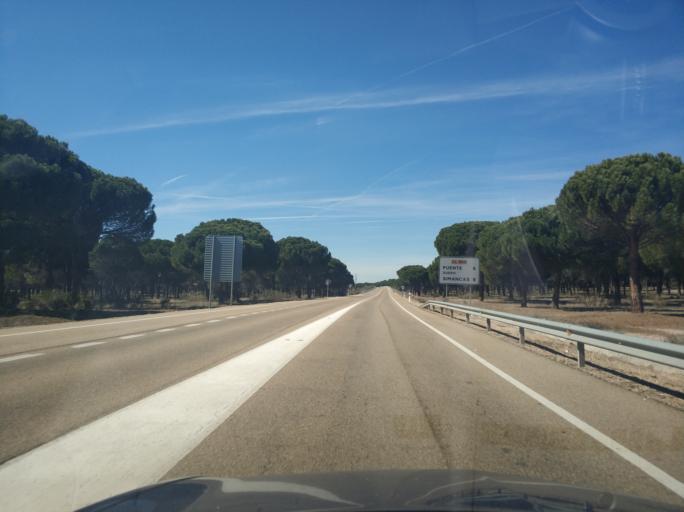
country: ES
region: Castille and Leon
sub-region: Provincia de Valladolid
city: Viana de Cega
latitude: 41.5325
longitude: -4.7301
